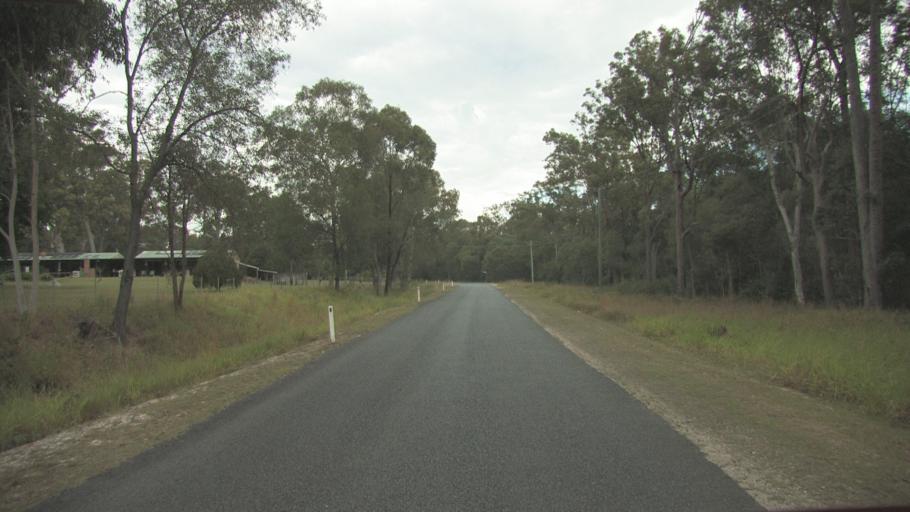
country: AU
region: Queensland
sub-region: Logan
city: Chambers Flat
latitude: -27.7856
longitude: 153.1090
